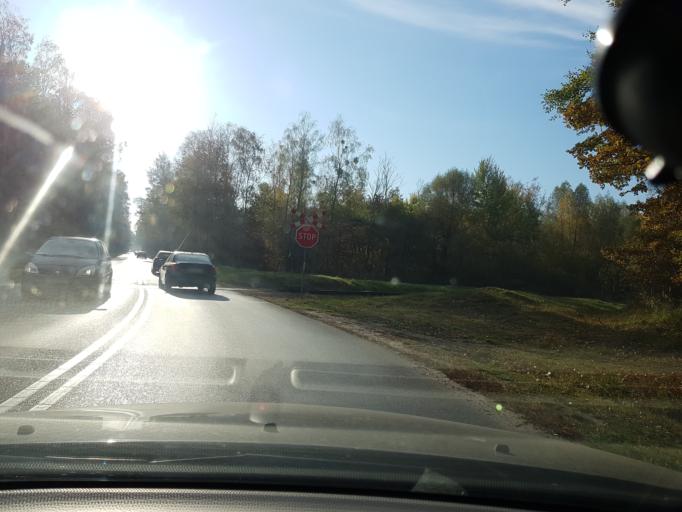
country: PL
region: Masovian Voivodeship
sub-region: Powiat warszawski zachodni
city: Babice
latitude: 52.2703
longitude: 20.8735
